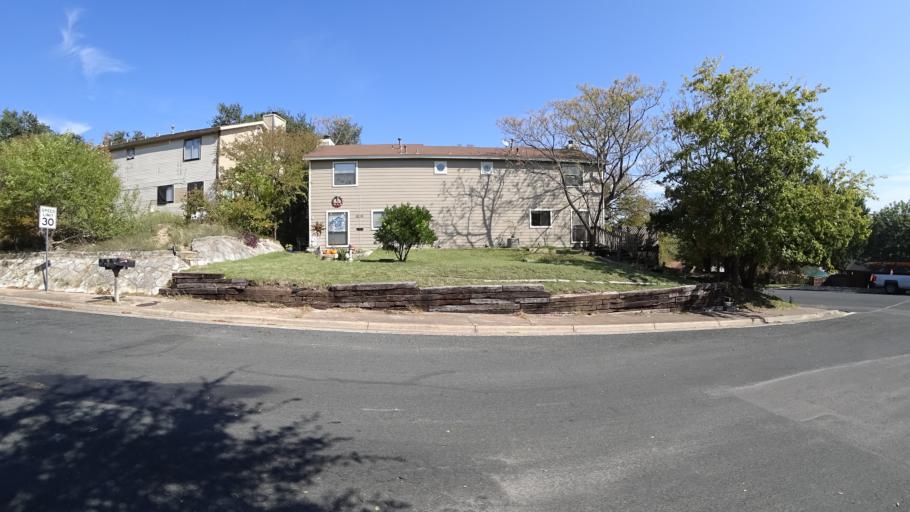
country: US
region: Texas
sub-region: Travis County
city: Shady Hollow
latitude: 30.2102
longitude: -97.8167
